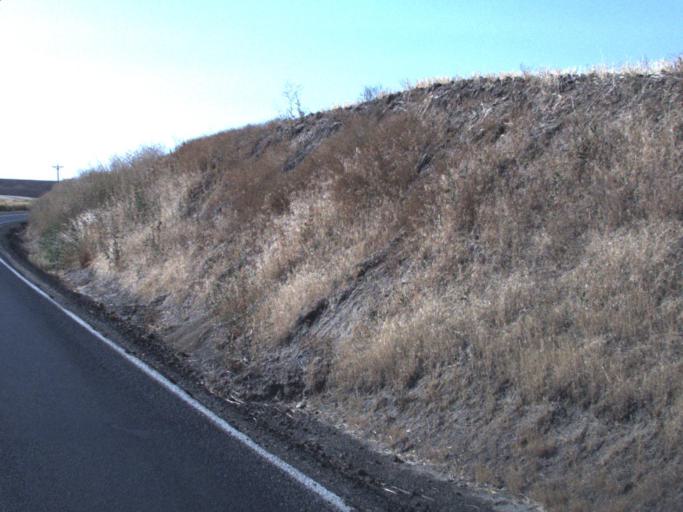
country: US
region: Washington
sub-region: Whitman County
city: Colfax
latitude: 47.1710
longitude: -117.2026
